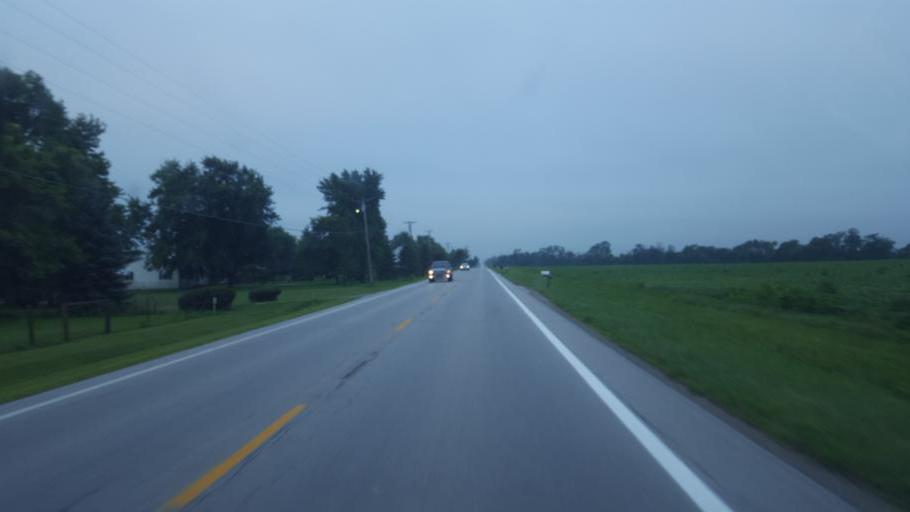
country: US
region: Ohio
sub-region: Madison County
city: Bethel
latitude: 39.6308
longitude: -83.3493
